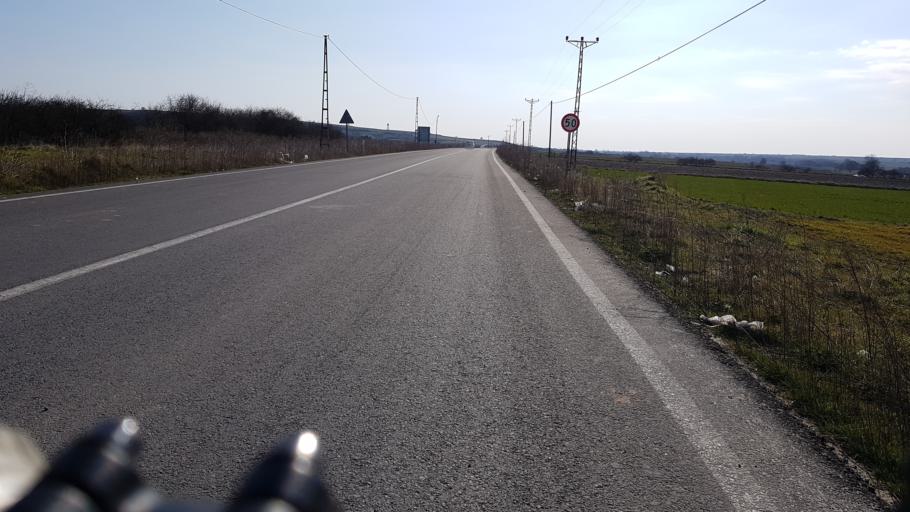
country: TR
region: Tekirdag
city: Saray
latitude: 41.3685
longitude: 27.8612
